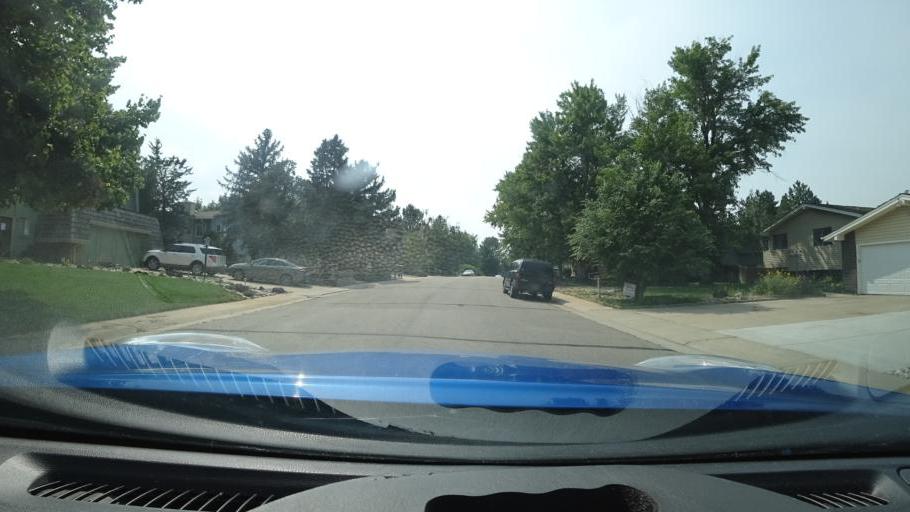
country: US
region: Colorado
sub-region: Adams County
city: Aurora
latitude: 39.6706
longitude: -104.8529
